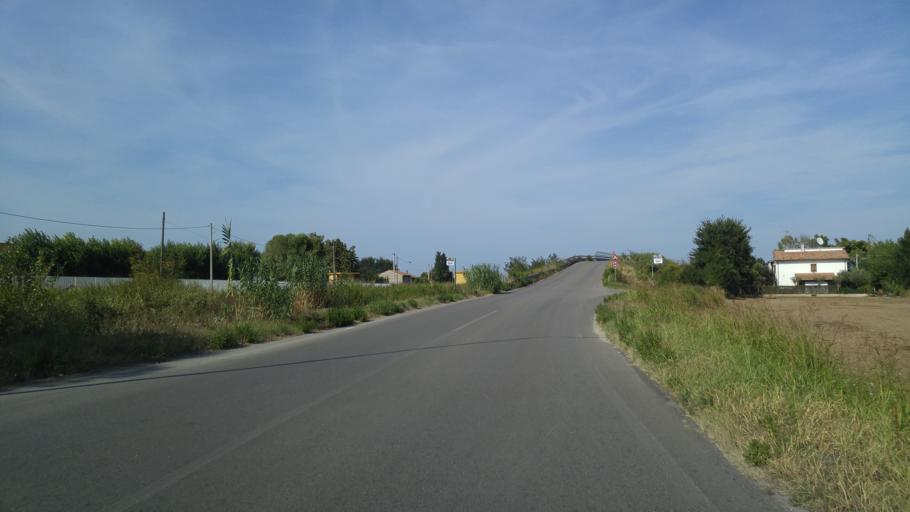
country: IT
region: The Marches
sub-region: Provincia di Pesaro e Urbino
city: Rosciano
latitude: 43.8144
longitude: 13.0071
